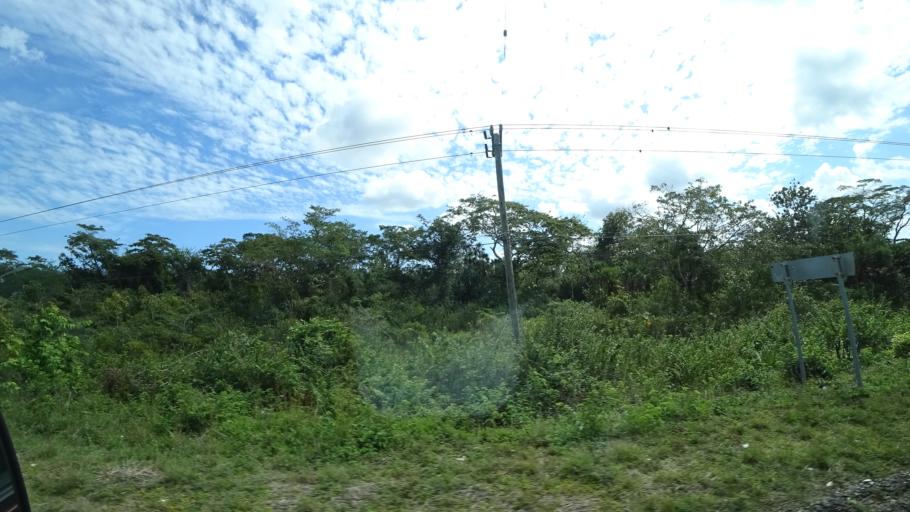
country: BZ
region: Belize
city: Belize City
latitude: 17.5689
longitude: -88.3882
